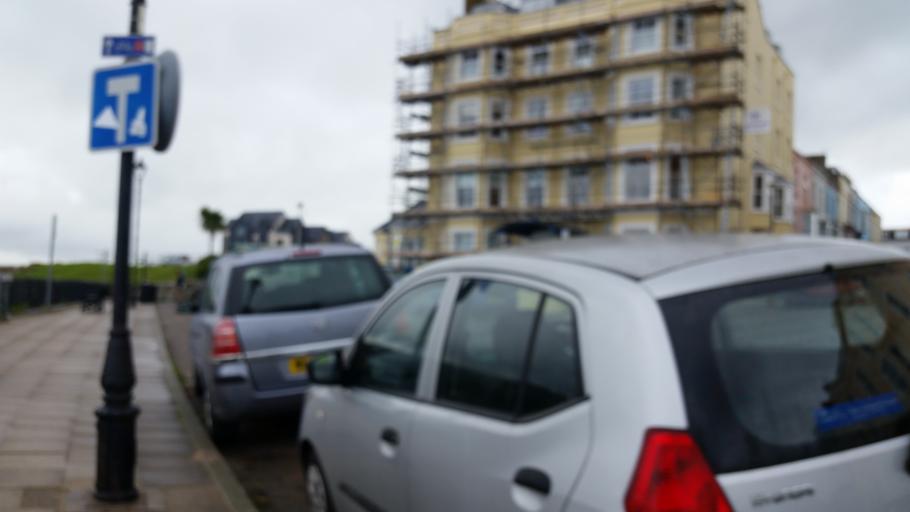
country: GB
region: Wales
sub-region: Pembrokeshire
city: Tenby
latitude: 51.6688
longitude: -4.7017
